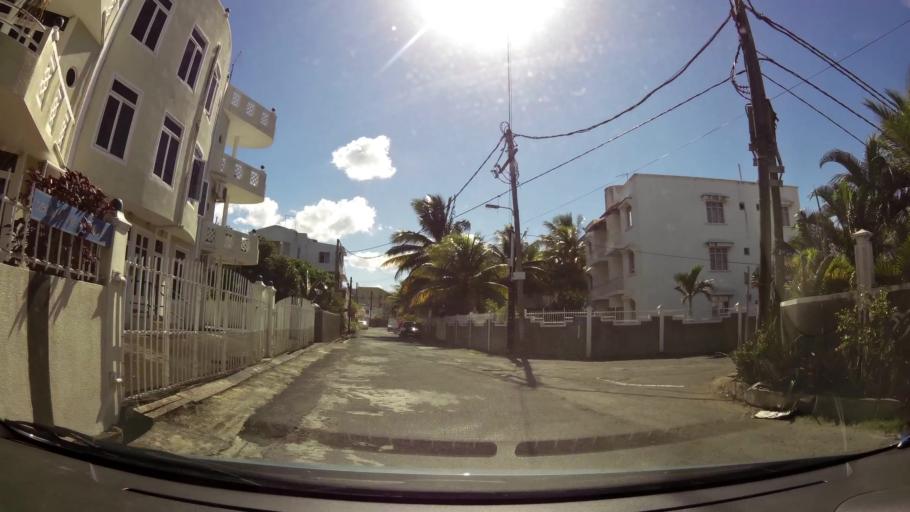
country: MU
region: Black River
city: Flic en Flac
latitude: -20.2899
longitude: 57.3644
